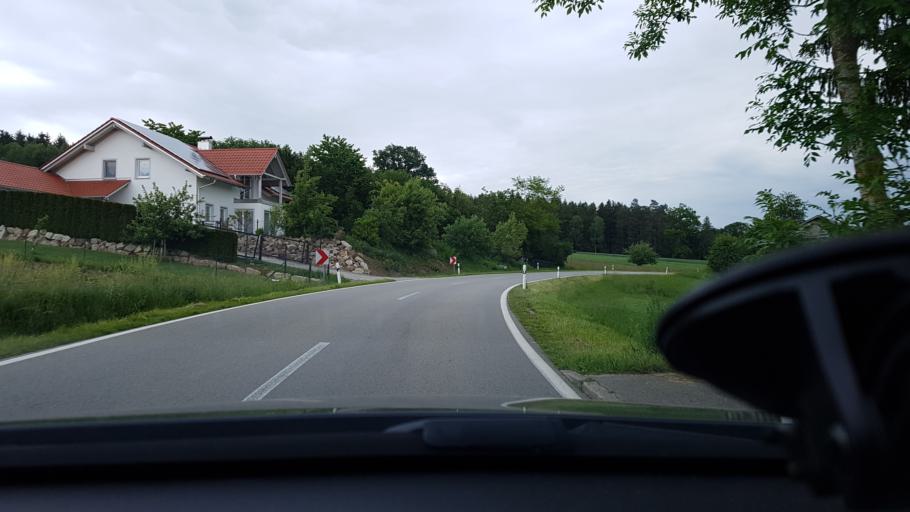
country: DE
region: Bavaria
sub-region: Lower Bavaria
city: Wittibreut
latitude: 48.3477
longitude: 13.0255
